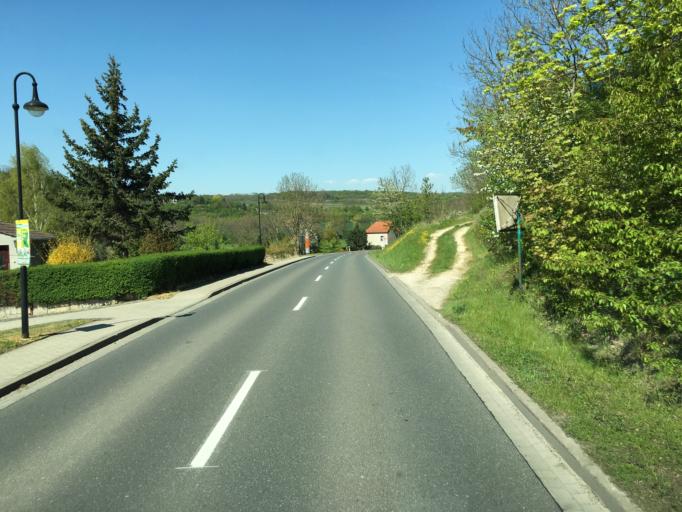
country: DE
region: Saxony-Anhalt
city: Balgstadt
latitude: 51.2070
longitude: 11.7393
